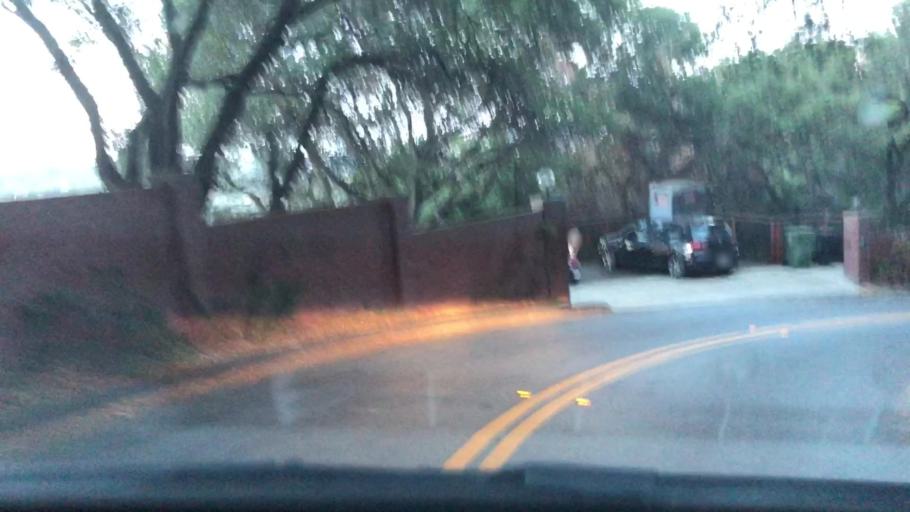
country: US
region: California
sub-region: Contra Costa County
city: Orinda
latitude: 37.8838
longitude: -122.2061
